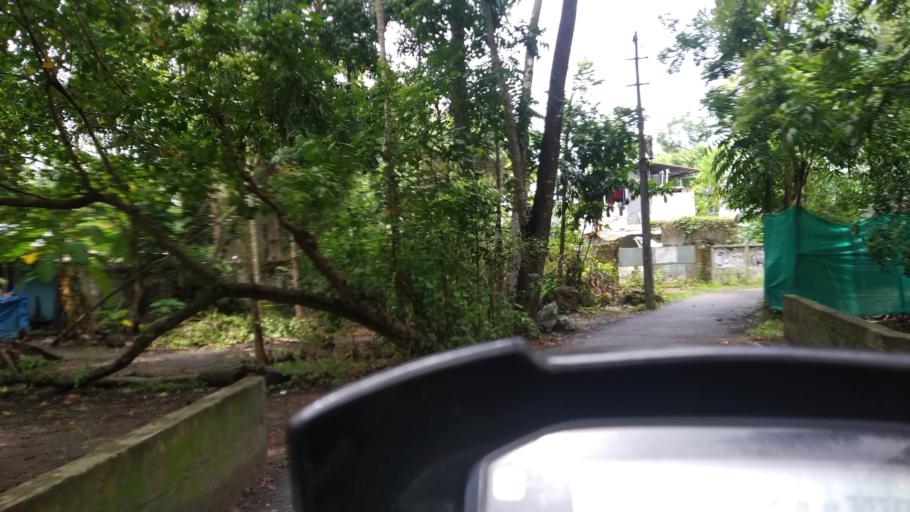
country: IN
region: Kerala
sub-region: Ernakulam
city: Elur
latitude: 10.0636
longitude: 76.2093
